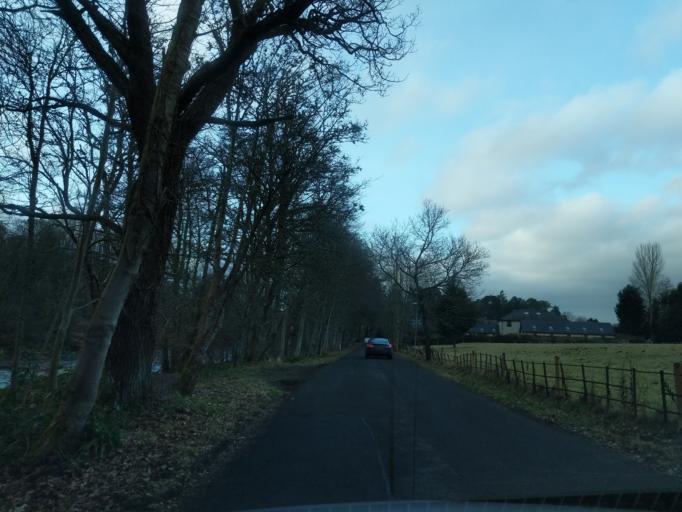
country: GB
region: Scotland
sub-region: South Lanarkshire
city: Carluke
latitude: 55.6945
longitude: -3.8646
